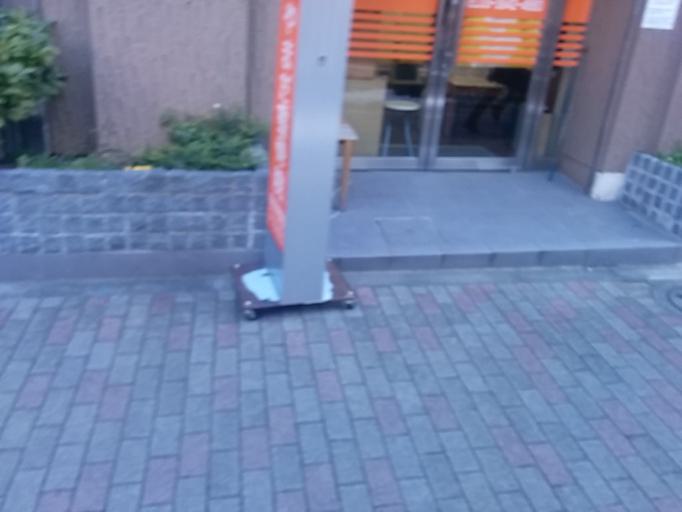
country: JP
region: Tokyo
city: Tokyo
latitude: 35.7308
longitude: 139.7506
